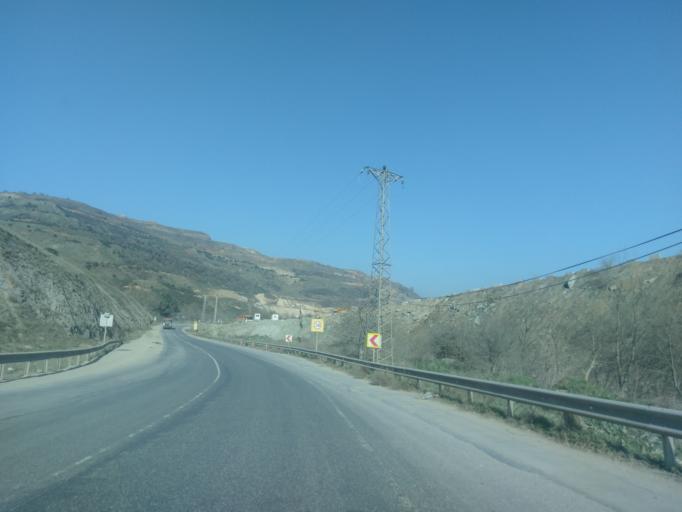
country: TR
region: Istanbul
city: Catalca
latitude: 41.1201
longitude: 28.4596
